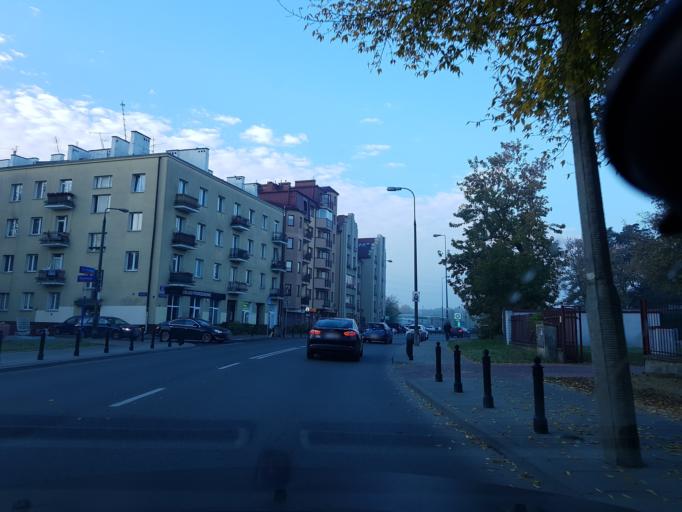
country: PL
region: Masovian Voivodeship
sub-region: Warszawa
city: Praga Polnoc
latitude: 52.2701
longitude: 21.0414
